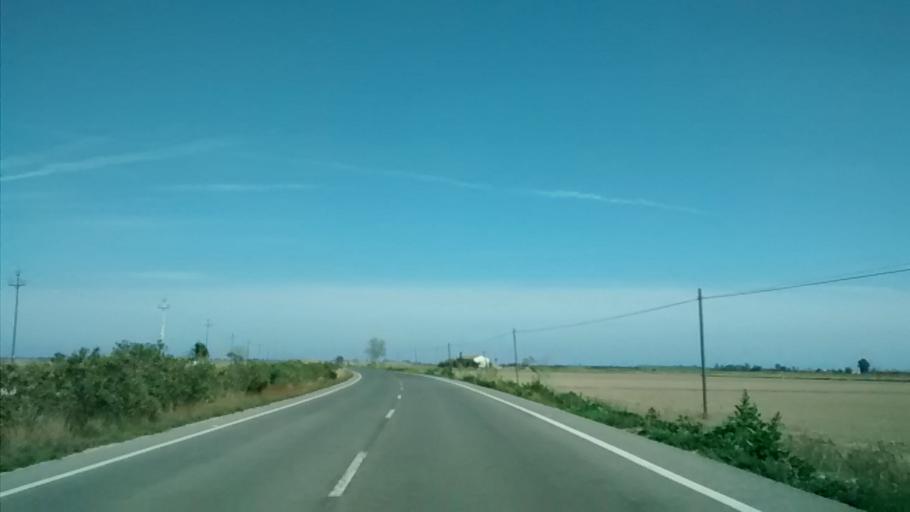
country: ES
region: Catalonia
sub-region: Provincia de Tarragona
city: Deltebre
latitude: 40.7067
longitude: 0.7661
